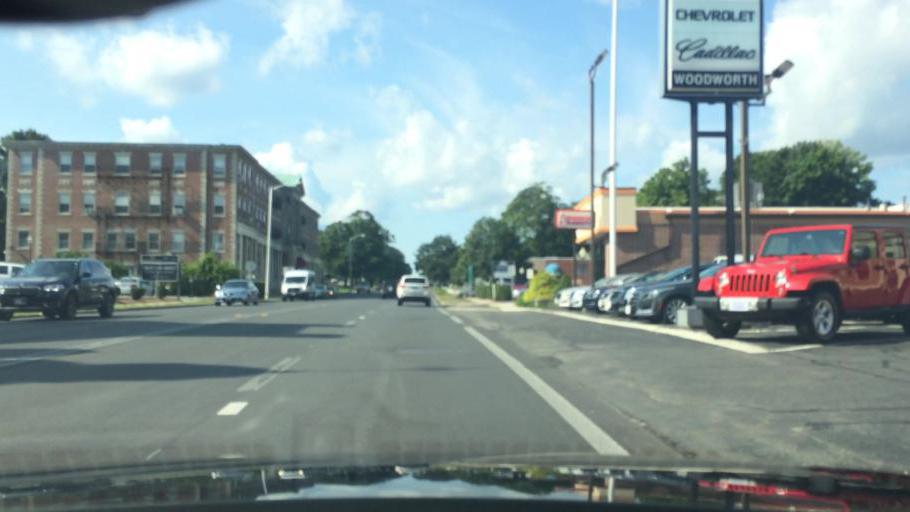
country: US
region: Massachusetts
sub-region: Essex County
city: Andover
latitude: 42.6726
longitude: -71.1507
